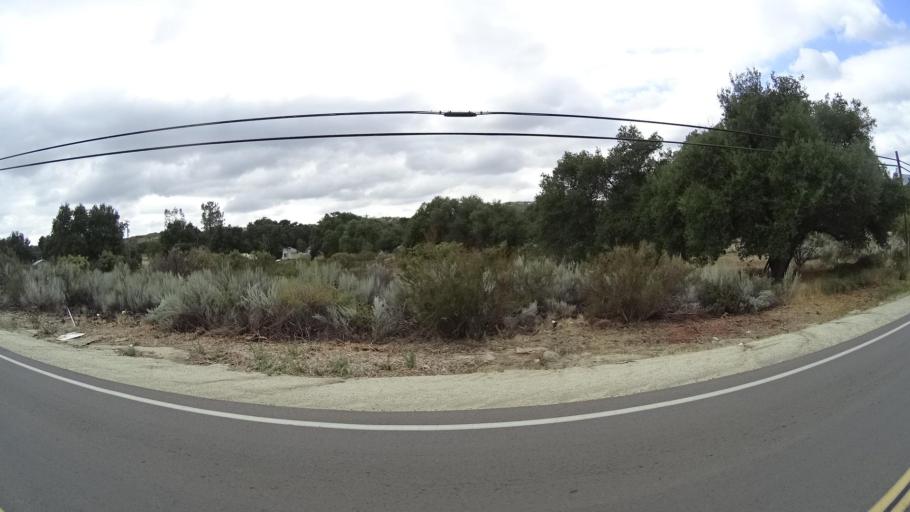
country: US
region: California
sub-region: San Diego County
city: Campo
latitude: 32.6753
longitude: -116.5061
